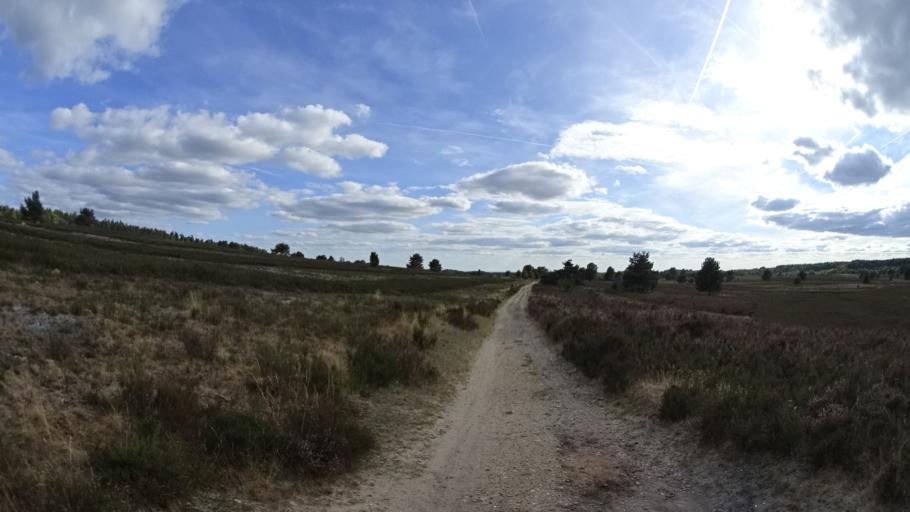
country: DE
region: Lower Saxony
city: Undeloh
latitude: 53.1642
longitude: 9.9329
